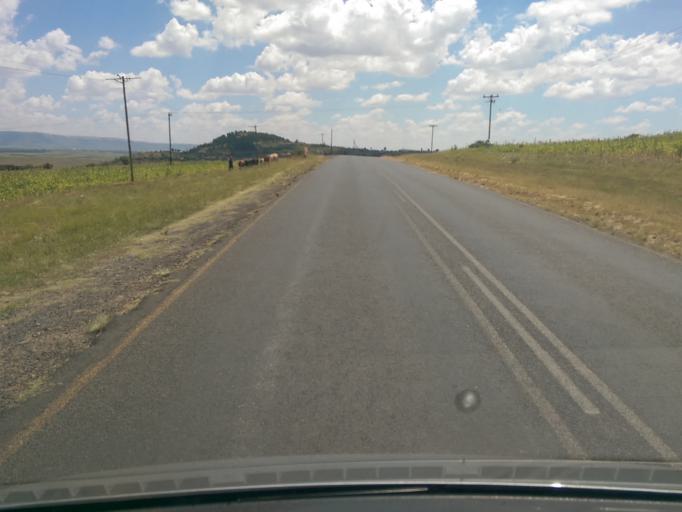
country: LS
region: Maseru
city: Nako
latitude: -29.4361
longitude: 27.6815
